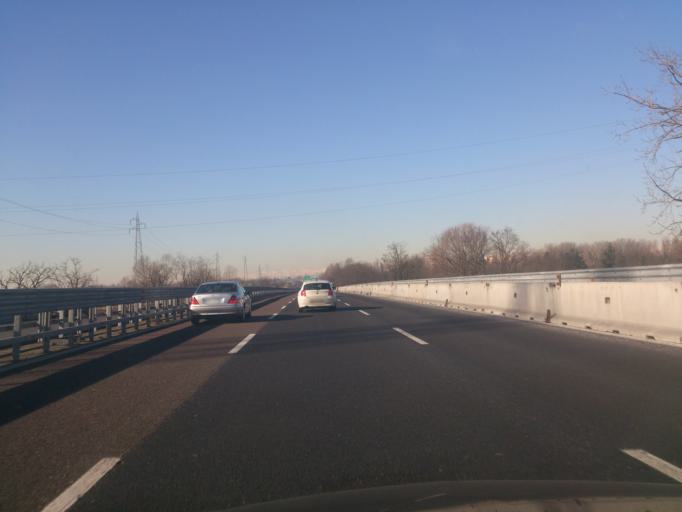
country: IT
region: Lombardy
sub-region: Citta metropolitana di Milano
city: Poasco-Sorigherio
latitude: 45.3861
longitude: 9.2308
